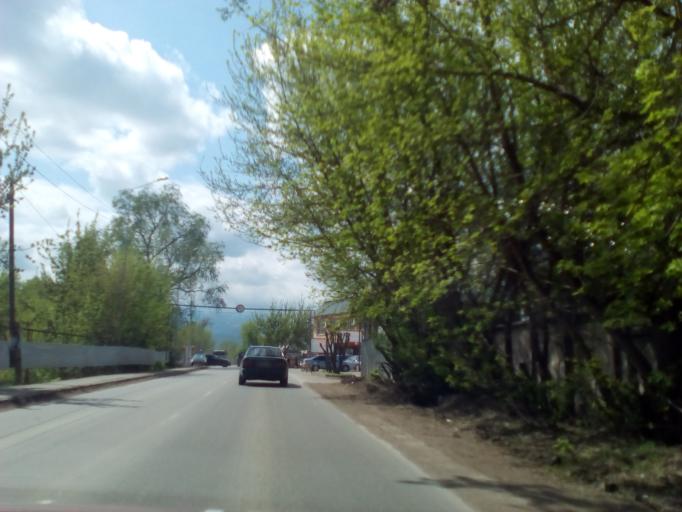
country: KZ
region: Almaty Oblysy
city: Burunday
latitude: 43.2479
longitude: 76.7623
